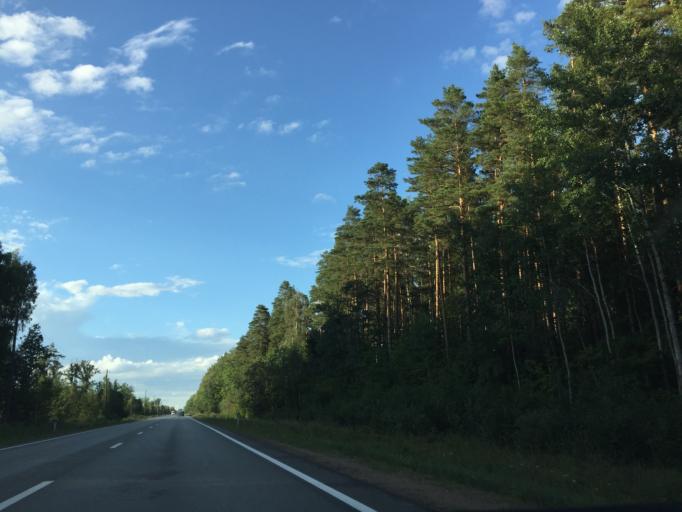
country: LV
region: Jelgava
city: Jelgava
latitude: 56.5532
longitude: 23.7103
